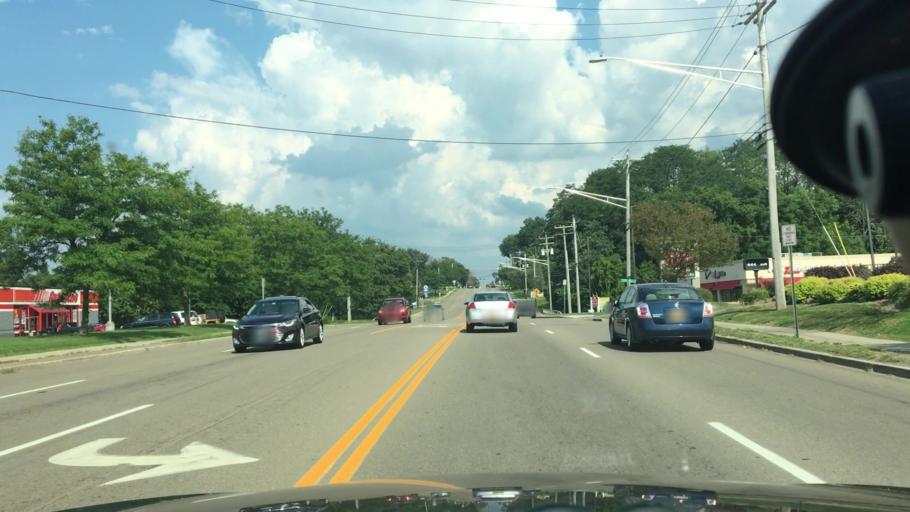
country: US
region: New York
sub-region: Chautauqua County
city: Jamestown West
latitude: 42.0974
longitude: -79.2903
